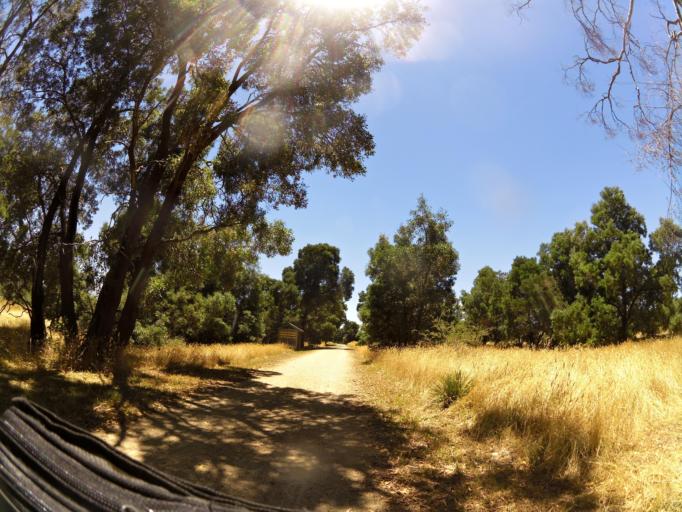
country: AU
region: Victoria
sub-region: Ballarat North
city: Delacombe
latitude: -37.6219
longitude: 143.7049
